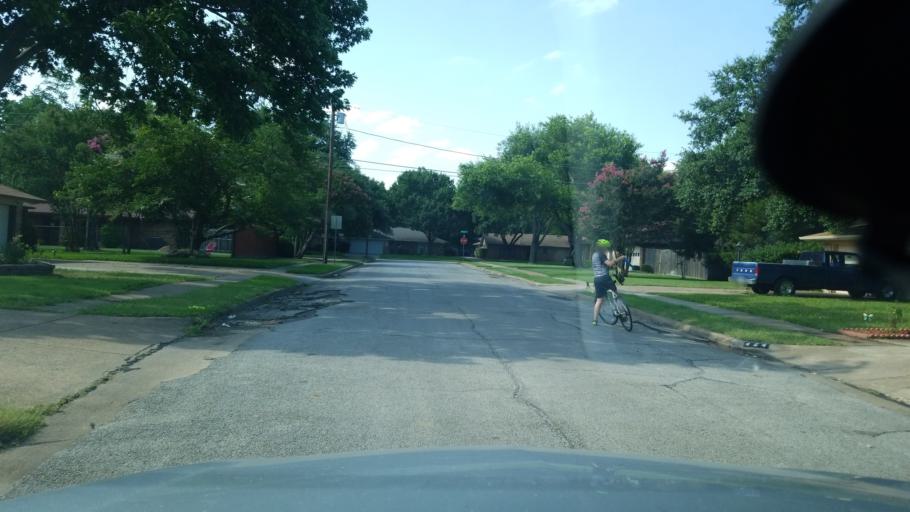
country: US
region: Texas
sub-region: Dallas County
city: Irving
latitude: 32.8192
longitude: -96.9727
